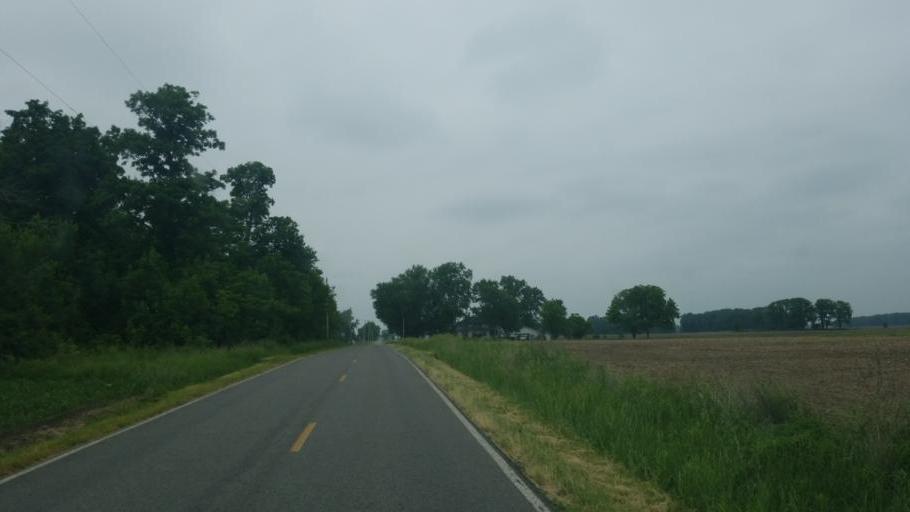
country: US
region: Indiana
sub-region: Marshall County
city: Bremen
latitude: 41.4918
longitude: -86.1178
